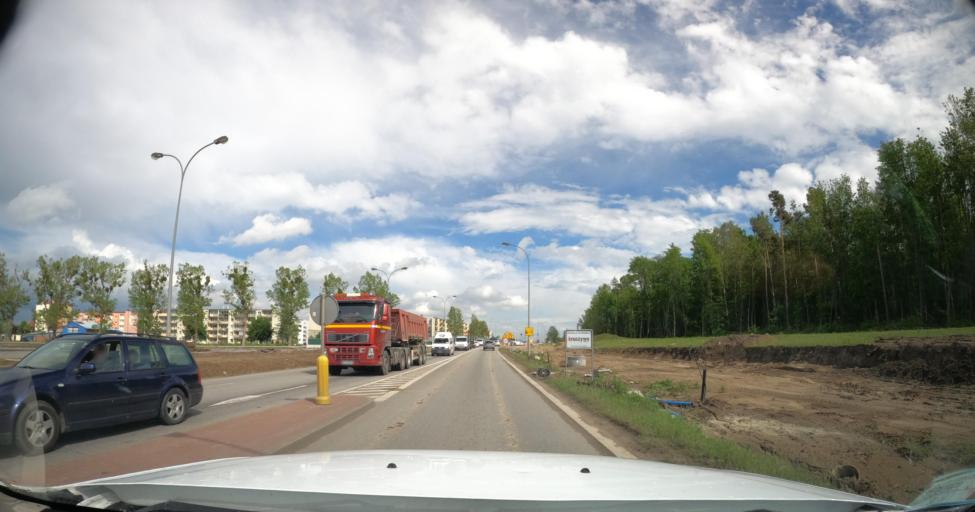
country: PL
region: Pomeranian Voivodeship
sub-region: Powiat gdanski
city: Lublewo Gdanskie
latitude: 54.3540
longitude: 18.4906
